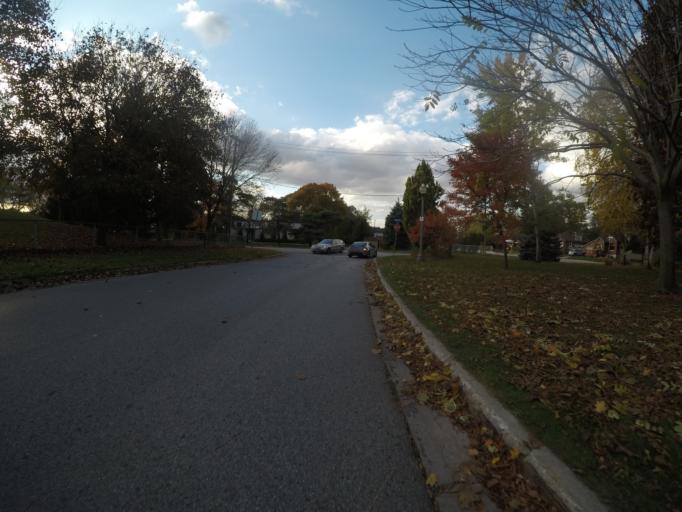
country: CA
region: Ontario
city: Kitchener
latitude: 43.4391
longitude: -80.4680
